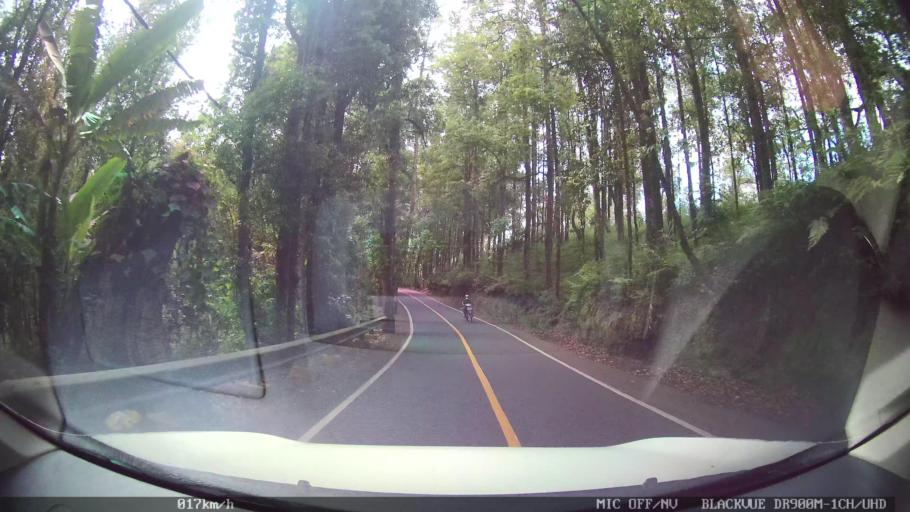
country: ID
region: Bali
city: Banjar Buahan
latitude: -8.2928
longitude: 115.3865
